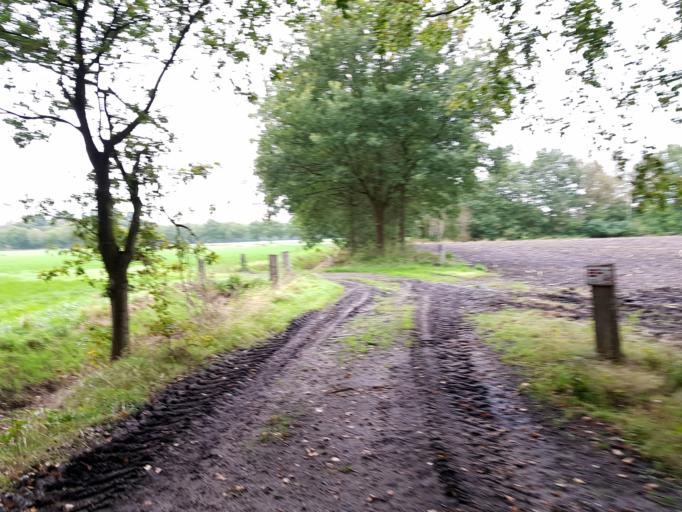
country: NL
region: Utrecht
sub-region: Gemeente Utrechtse Heuvelrug
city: Maarsbergen
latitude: 52.0536
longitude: 5.3994
